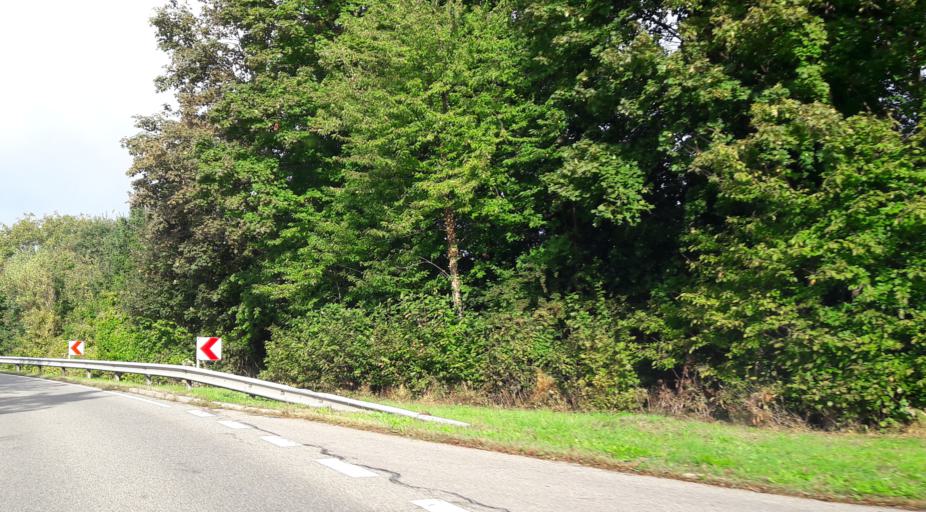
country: DE
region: Baden-Wuerttemberg
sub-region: Regierungsbezirk Stuttgart
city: Ittlingen
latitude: 49.2292
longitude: 8.9295
